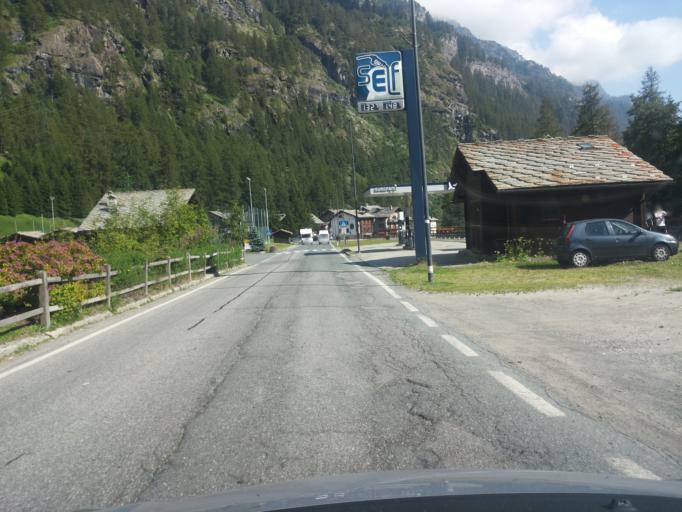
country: IT
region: Aosta Valley
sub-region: Valle d'Aosta
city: Gressoney-La-Trinite
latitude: 45.8298
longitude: 7.8239
